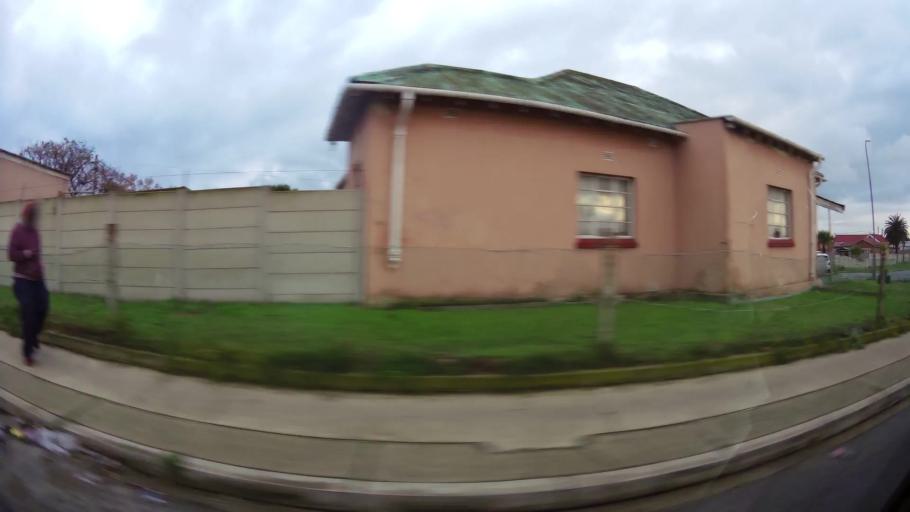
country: ZA
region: Eastern Cape
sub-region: Nelson Mandela Bay Metropolitan Municipality
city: Port Elizabeth
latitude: -33.9253
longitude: 25.6033
